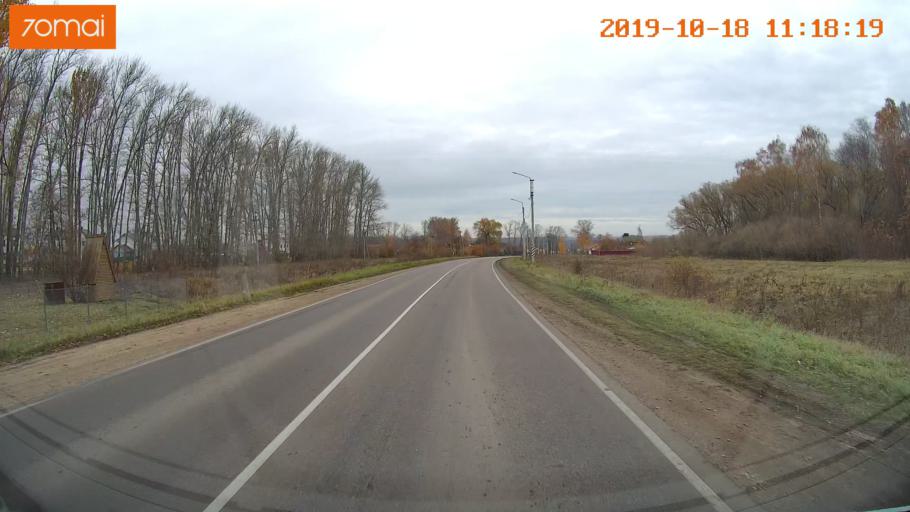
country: RU
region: Tula
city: Kimovsk
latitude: 54.0378
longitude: 38.5502
